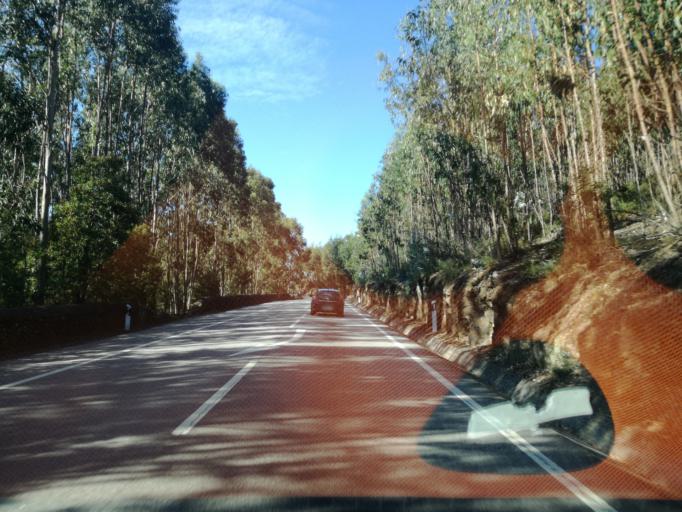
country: PT
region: Porto
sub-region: Pacos de Ferreira
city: Seroa
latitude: 41.2593
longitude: -8.4608
